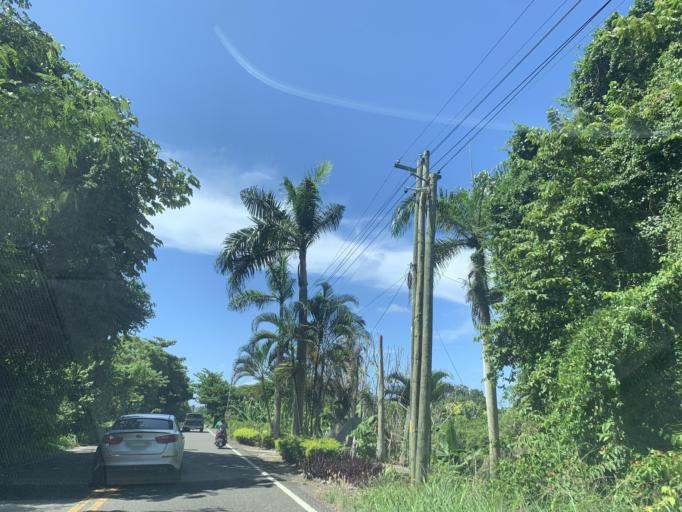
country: DO
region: Maria Trinidad Sanchez
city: Cabrera
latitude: 19.6607
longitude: -69.9390
